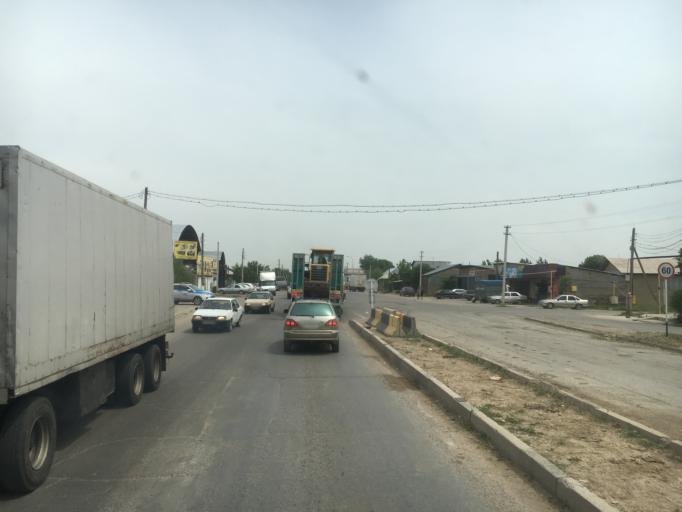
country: KZ
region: Ongtustik Qazaqstan
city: Shymkent
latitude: 42.3369
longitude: 69.5191
